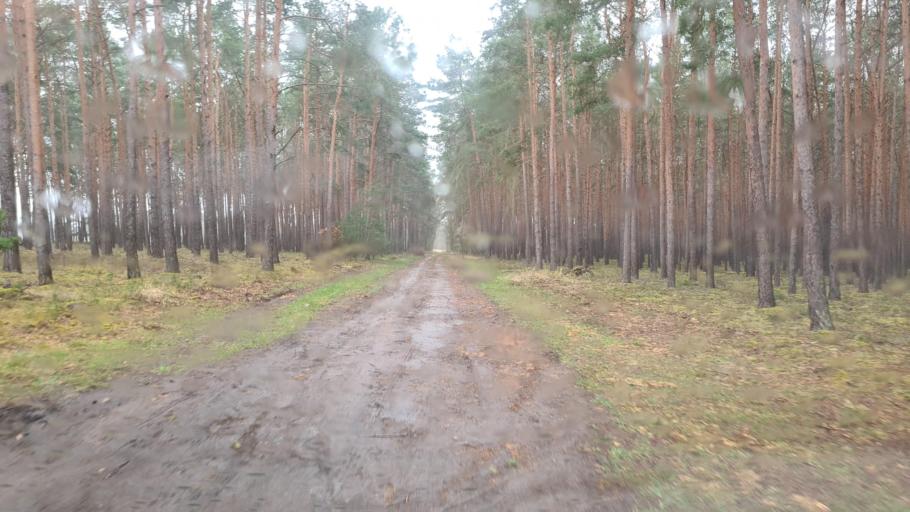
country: DE
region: Brandenburg
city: Bruck
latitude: 52.1640
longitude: 12.7221
